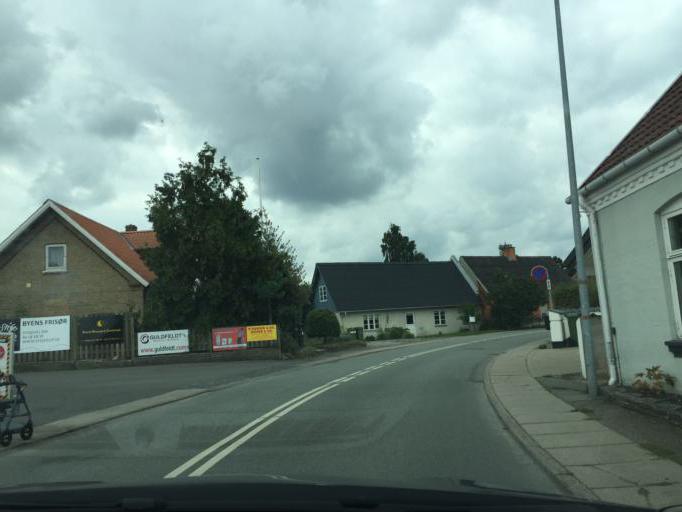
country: DK
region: South Denmark
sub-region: Odense Kommune
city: Stige
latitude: 55.4371
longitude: 10.4107
